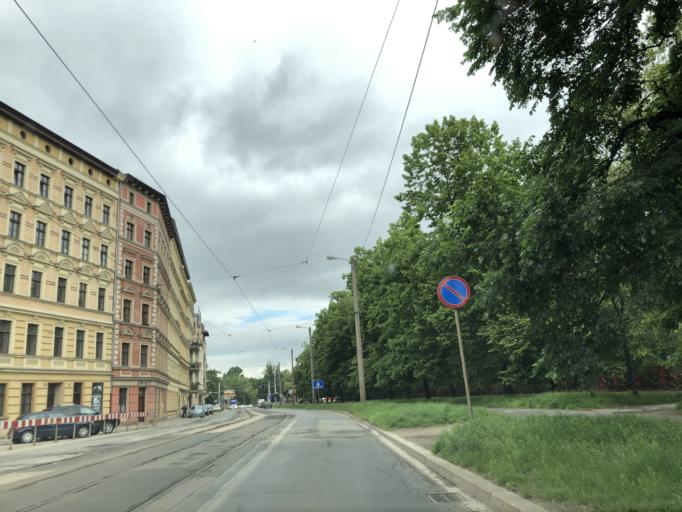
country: PL
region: Lower Silesian Voivodeship
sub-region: Powiat wroclawski
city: Wroclaw
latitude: 51.1239
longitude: 17.0295
